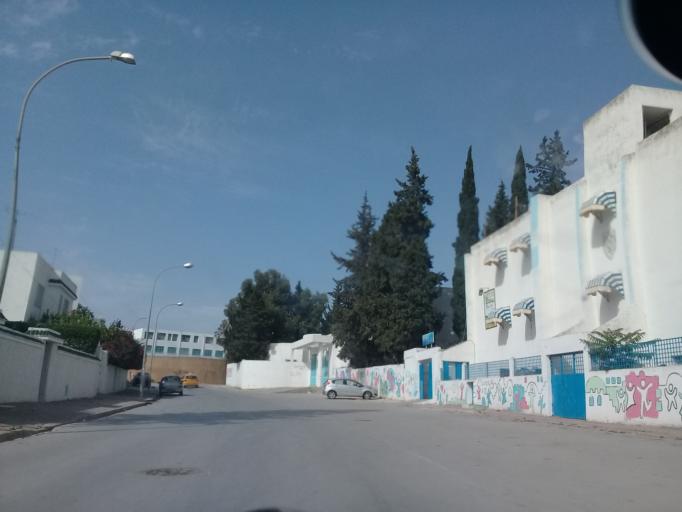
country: TN
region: Tunis
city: Tunis
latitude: 36.8504
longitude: 10.1618
